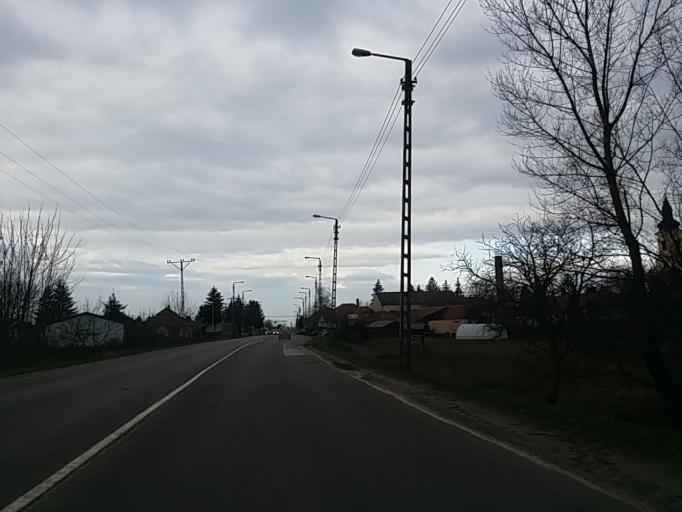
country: HU
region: Heves
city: Kompolt
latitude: 47.7588
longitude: 20.2495
